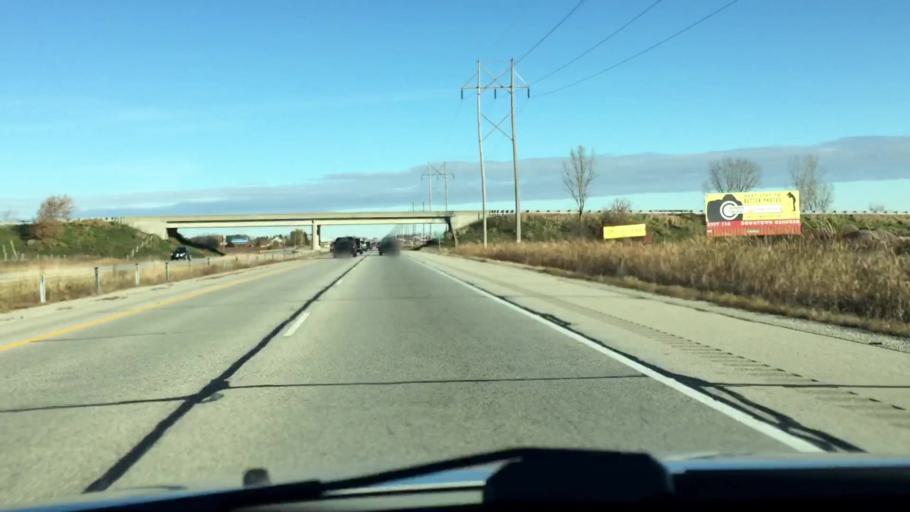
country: US
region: Wisconsin
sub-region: Winnebago County
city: Oshkosh
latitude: 43.9075
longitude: -88.5835
